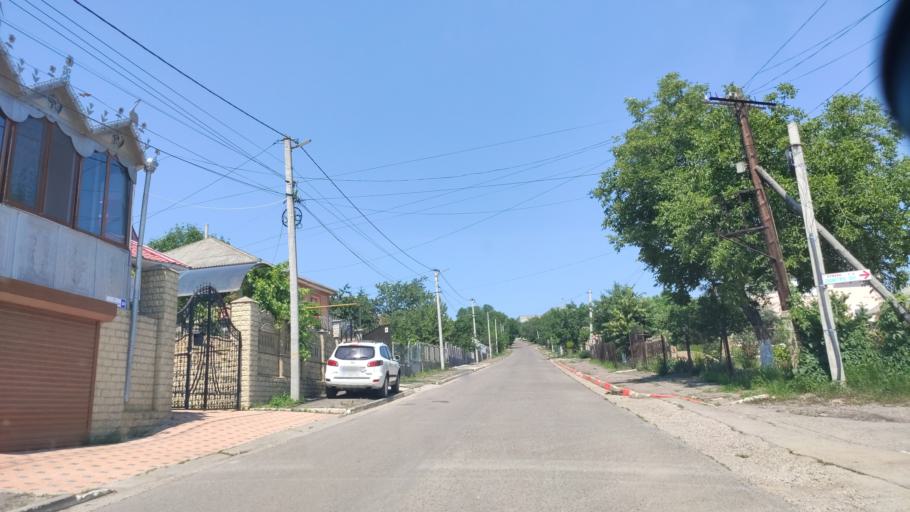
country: MD
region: Raionul Soroca
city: Soroca
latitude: 48.1698
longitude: 28.2989
